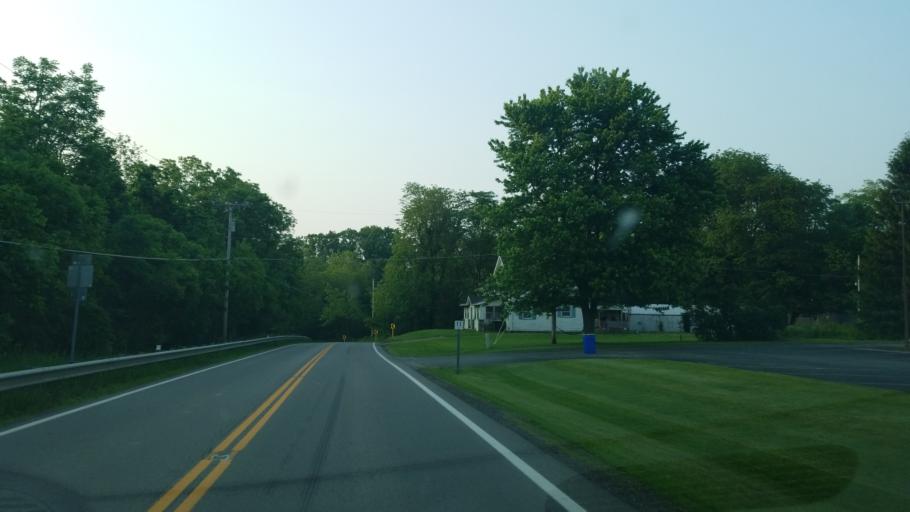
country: US
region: Ohio
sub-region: Ashland County
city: Ashland
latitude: 40.9342
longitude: -82.3150
